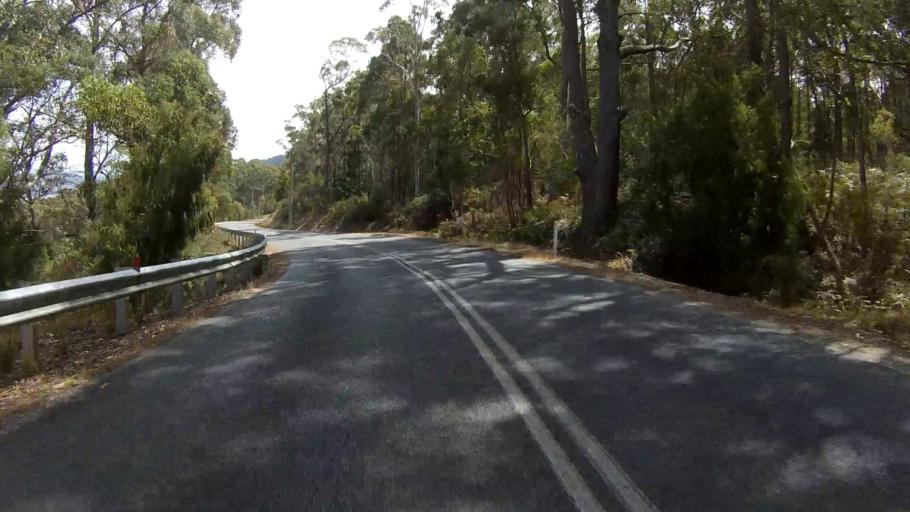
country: AU
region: Tasmania
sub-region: Huon Valley
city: Cygnet
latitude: -43.2233
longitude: 147.1283
